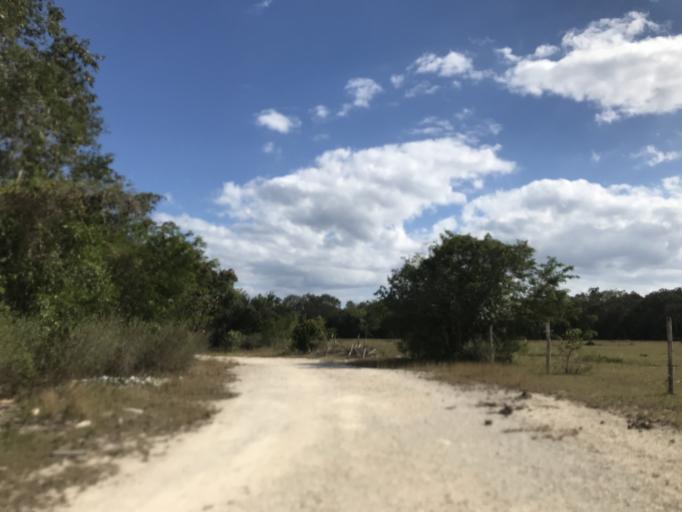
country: CU
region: Cienfuegos
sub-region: Municipio de Aguada de Pasajeros
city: Aguada de Pasajeros
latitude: 22.0760
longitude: -81.0381
